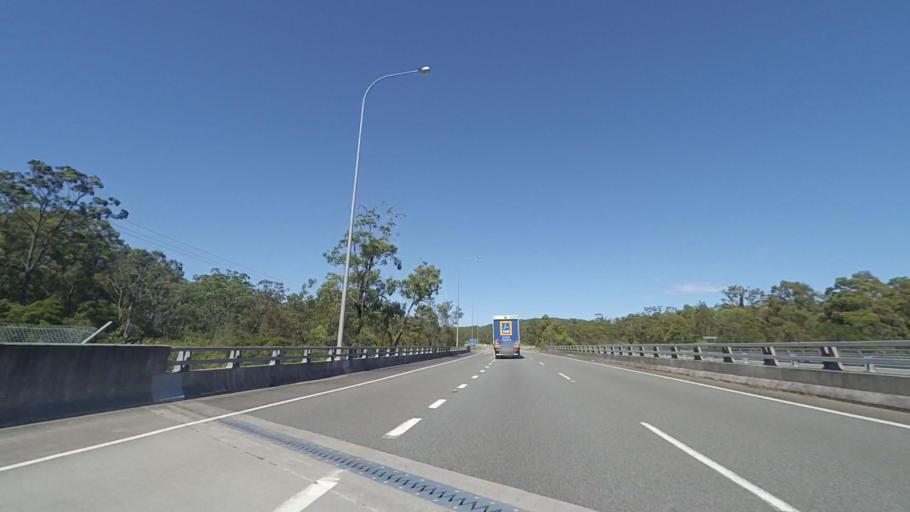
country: AU
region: New South Wales
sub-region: Port Stephens Shire
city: Port Stephens
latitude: -32.6114
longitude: 152.0858
